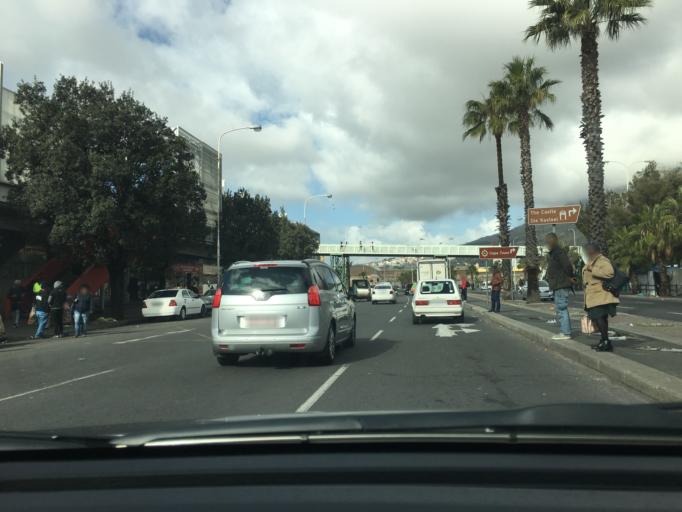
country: ZA
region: Western Cape
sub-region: City of Cape Town
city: Cape Town
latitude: -33.9235
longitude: 18.4253
